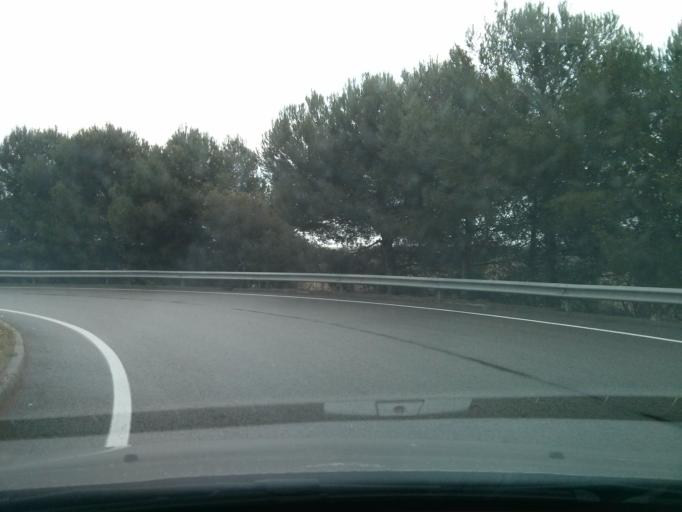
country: ES
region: Catalonia
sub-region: Provincia de Tarragona
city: El Vendrell
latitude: 41.1939
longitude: 1.5391
